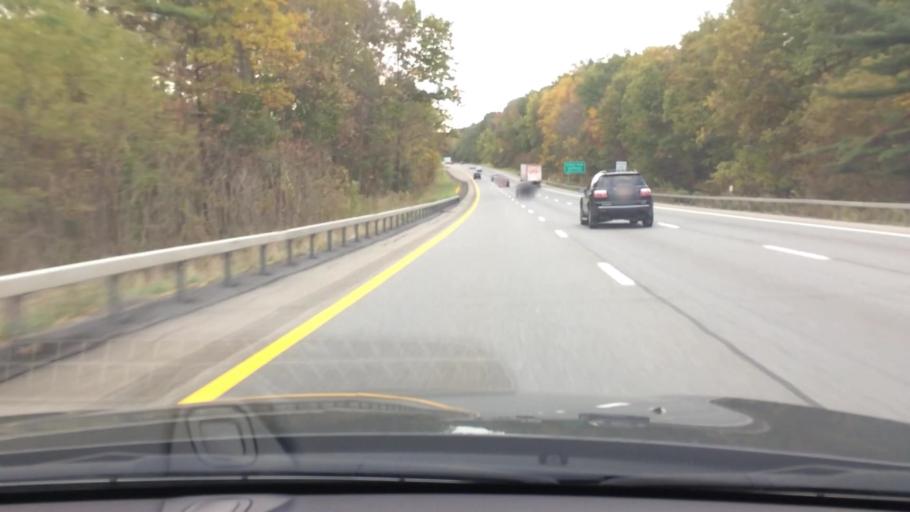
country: US
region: New York
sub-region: Saratoga County
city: Country Knolls
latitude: 42.9282
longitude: -73.8032
